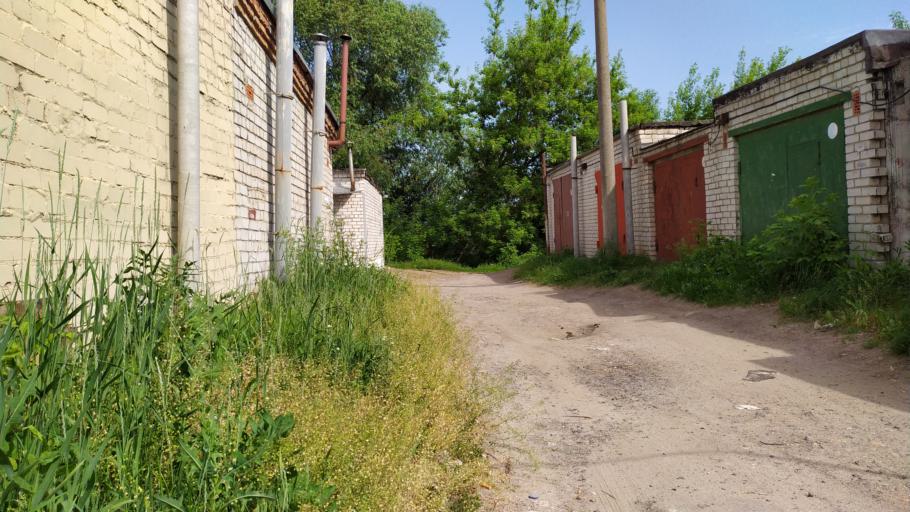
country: RU
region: Kursk
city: Kursk
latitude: 51.6631
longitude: 36.1524
